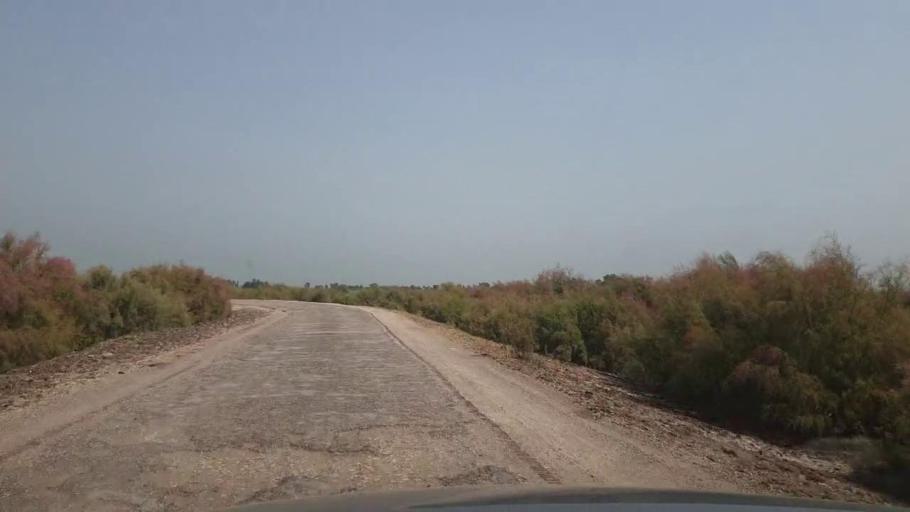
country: PK
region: Sindh
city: Madeji
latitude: 27.8322
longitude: 68.4469
